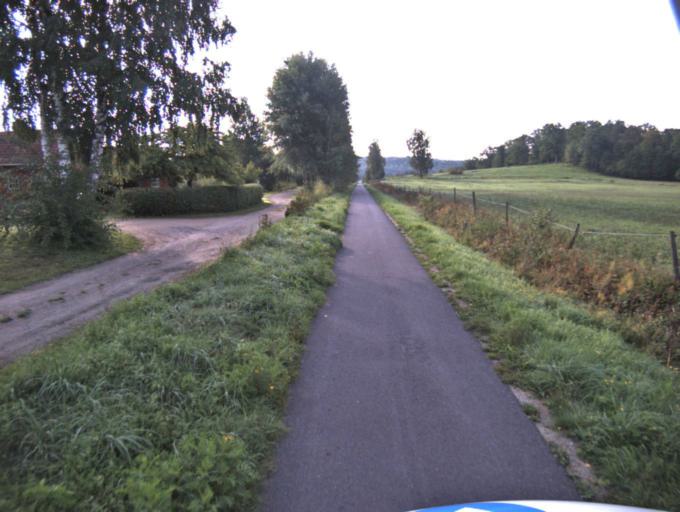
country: SE
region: Vaestra Goetaland
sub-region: Ulricehamns Kommun
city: Ulricehamn
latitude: 57.7405
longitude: 13.4004
